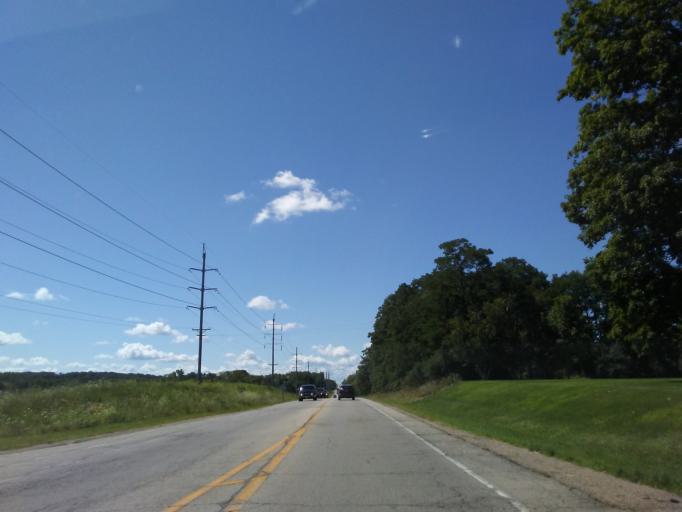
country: US
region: Wisconsin
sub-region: Dane County
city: Verona
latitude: 43.0239
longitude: -89.5335
